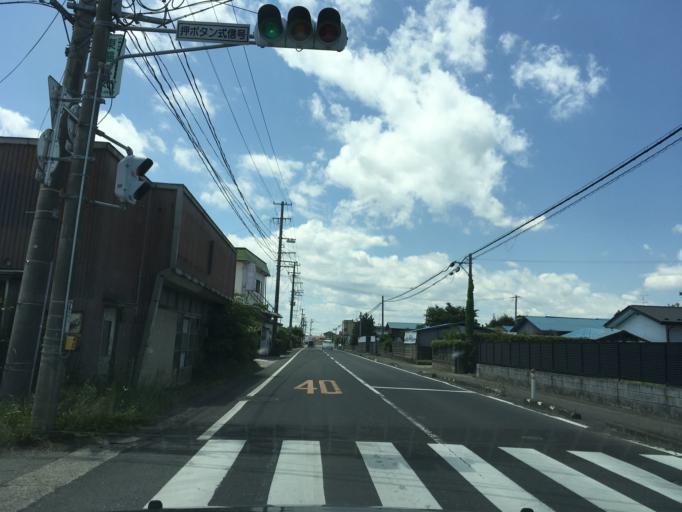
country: JP
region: Miyagi
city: Wakuya
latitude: 38.6791
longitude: 141.2172
